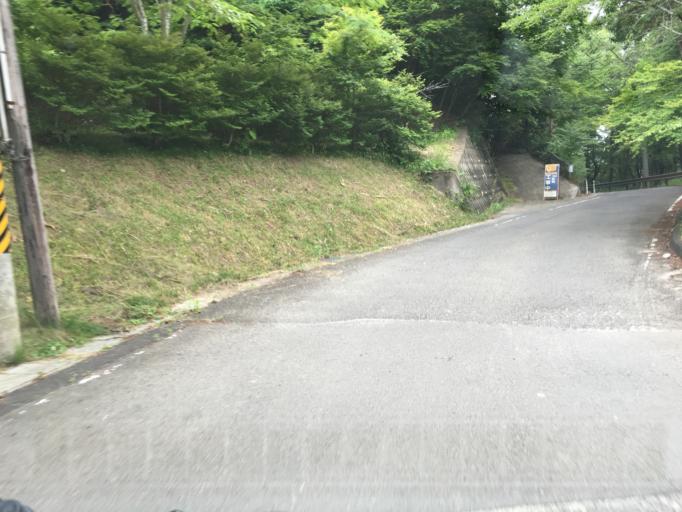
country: JP
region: Fukushima
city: Nihommatsu
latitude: 37.6436
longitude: 140.5291
